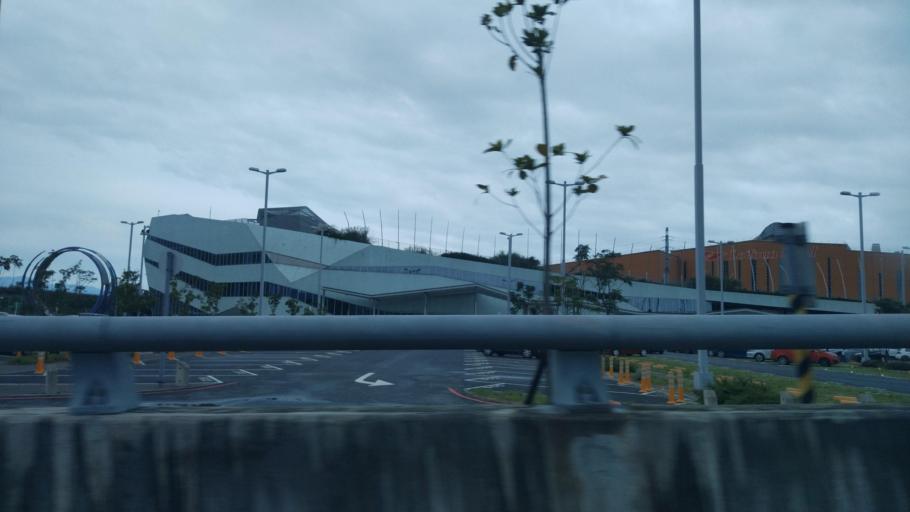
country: TW
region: Taiwan
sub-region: Yilan
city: Yilan
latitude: 24.6205
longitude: 121.8165
